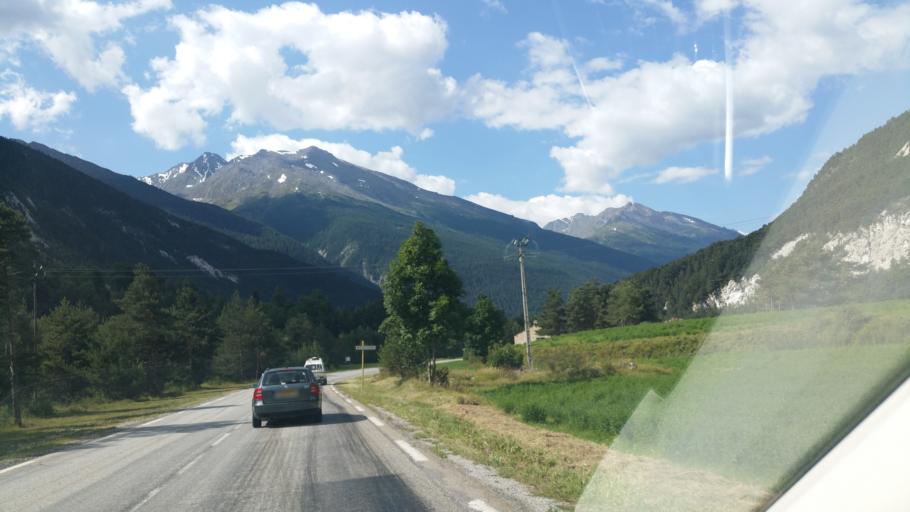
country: FR
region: Rhone-Alpes
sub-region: Departement de la Savoie
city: Modane
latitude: 45.2468
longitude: 6.7970
